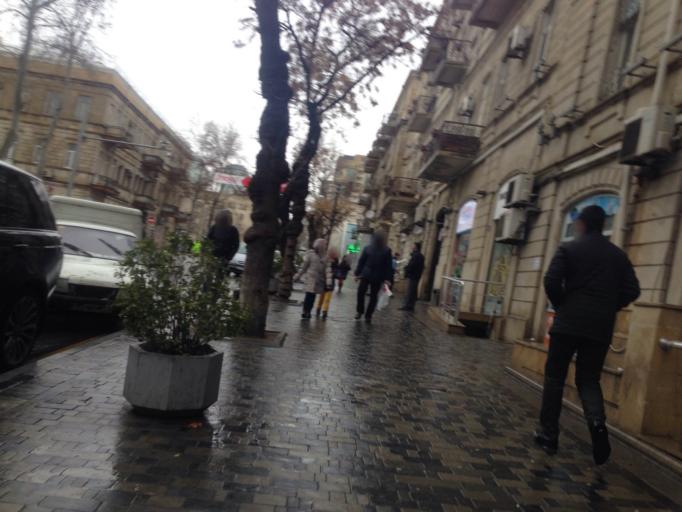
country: AZ
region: Baki
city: Baku
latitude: 40.3766
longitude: 49.8428
